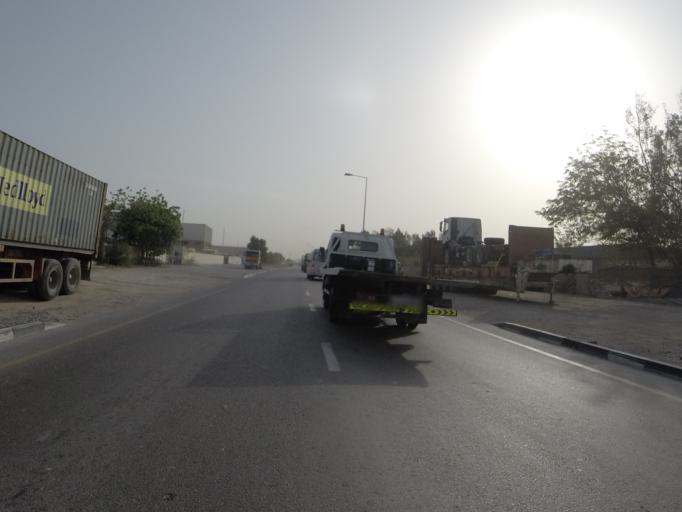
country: AE
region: Dubai
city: Dubai
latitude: 24.9682
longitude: 55.0692
